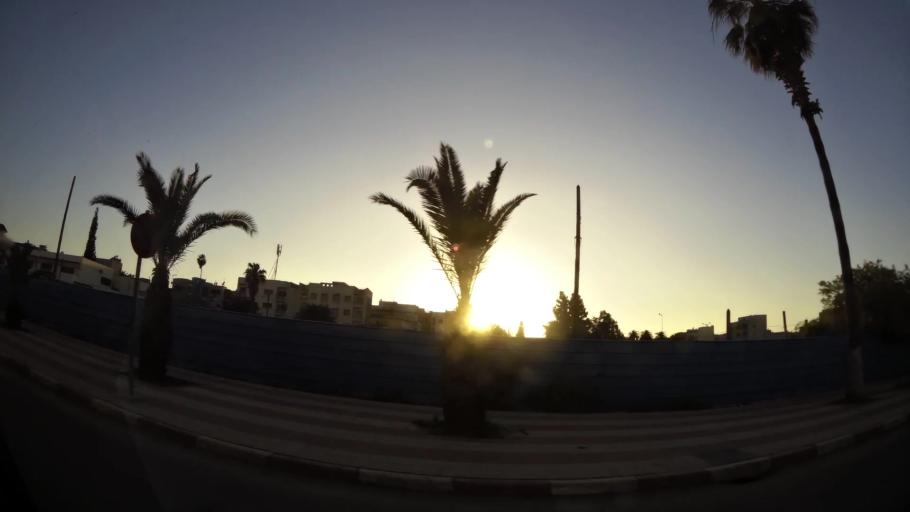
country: MA
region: Chaouia-Ouardigha
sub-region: Settat Province
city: Settat
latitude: 32.9990
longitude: -7.6204
